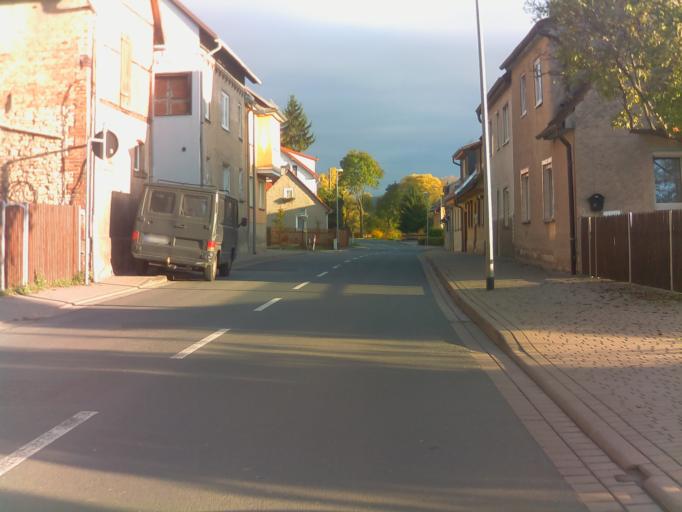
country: DE
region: Thuringia
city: Rittersdorf
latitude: 50.8569
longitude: 11.2520
